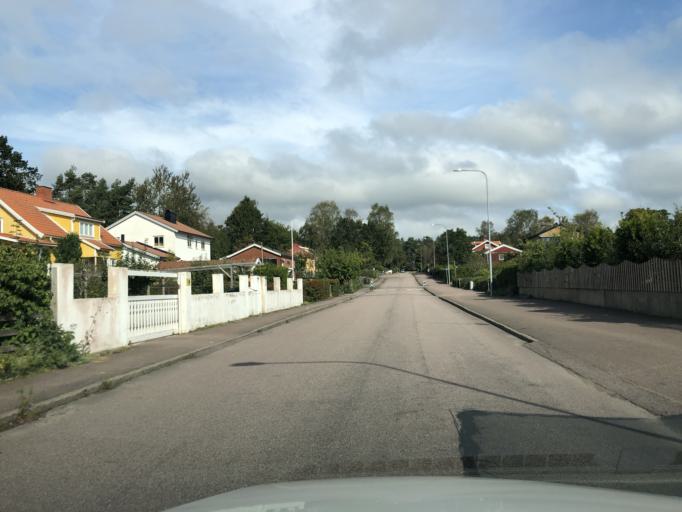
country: SE
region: Vaestra Goetaland
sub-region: Goteborg
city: Majorna
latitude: 57.7409
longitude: 11.9139
